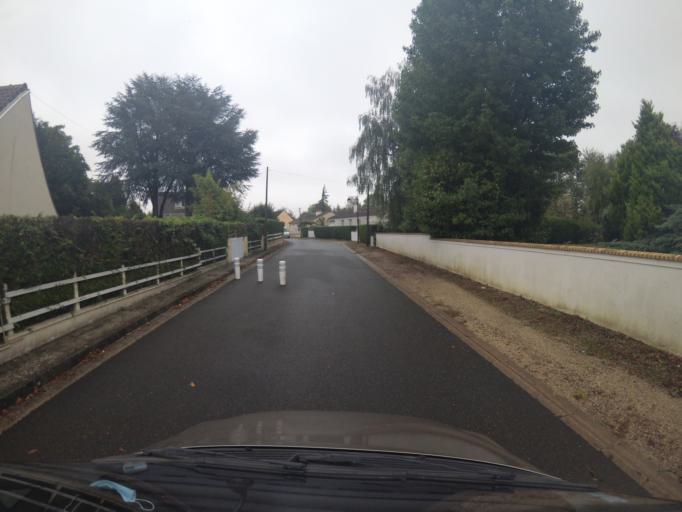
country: FR
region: Ile-de-France
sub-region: Departement de Seine-et-Marne
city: Chanteloup-en-Brie
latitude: 48.8397
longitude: 2.7567
